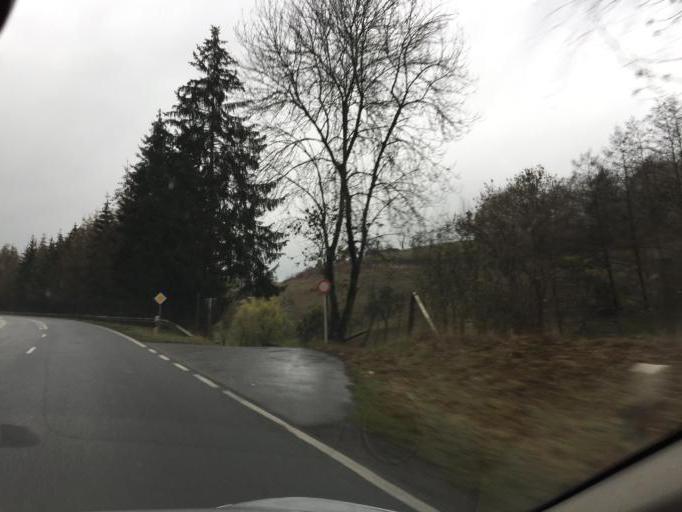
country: LU
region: Diekirch
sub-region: Canton de Diekirch
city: Diekirch
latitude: 49.8817
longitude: 6.1500
